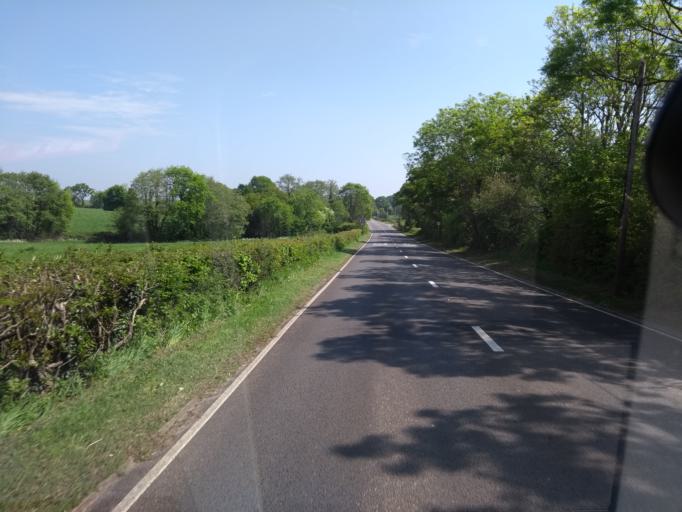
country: GB
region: England
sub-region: Somerset
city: Chard
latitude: 50.9216
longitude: -2.9892
